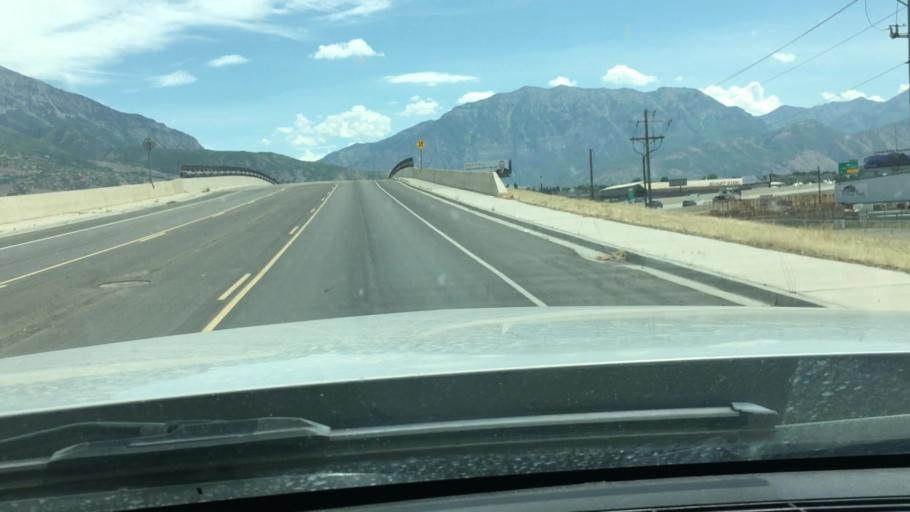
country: US
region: Utah
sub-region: Utah County
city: Lindon
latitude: 40.3330
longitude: -111.7448
